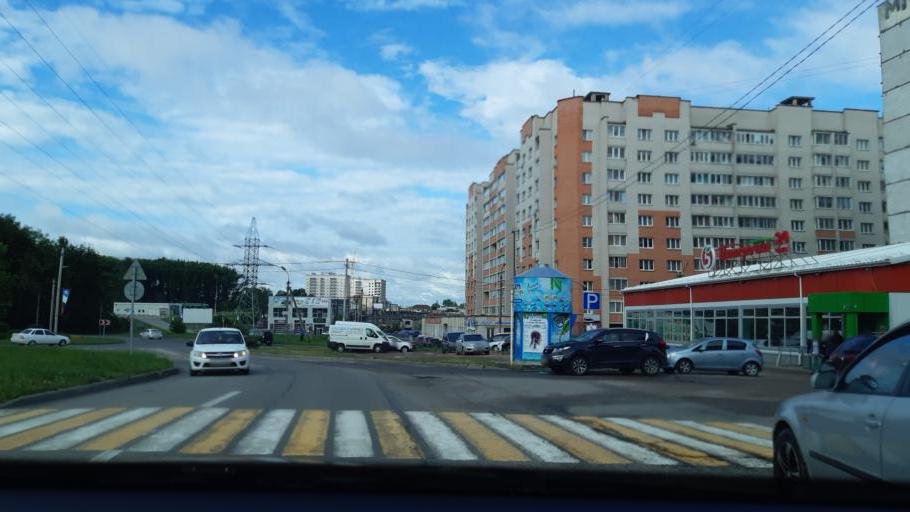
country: RU
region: Smolensk
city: Smolensk
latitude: 54.7614
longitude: 32.0843
